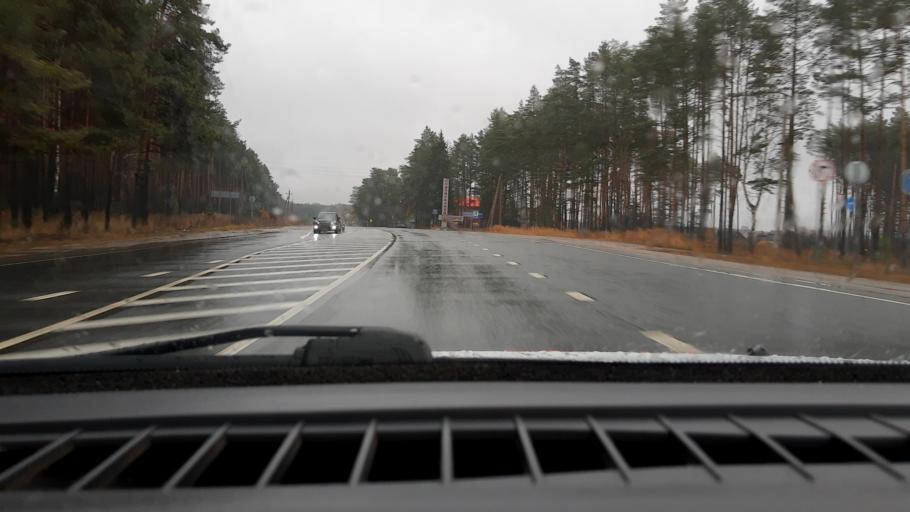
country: RU
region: Nizjnij Novgorod
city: Linda
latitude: 56.6857
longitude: 44.1783
